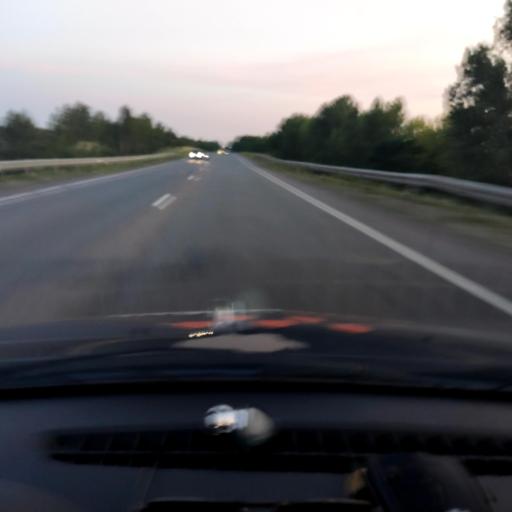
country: RU
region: Kursk
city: Gorshechnoye
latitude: 51.4438
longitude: 37.9101
